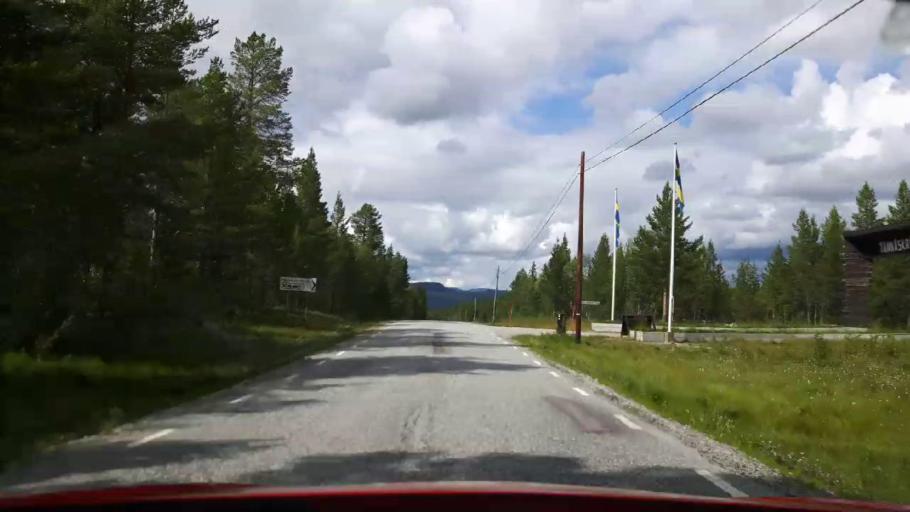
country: NO
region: Hedmark
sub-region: Engerdal
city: Engerdal
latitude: 62.4120
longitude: 12.7107
